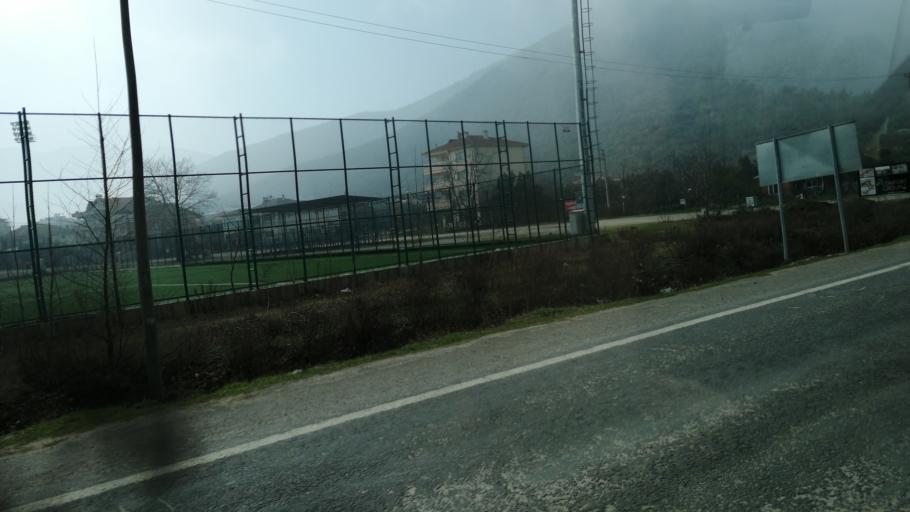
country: TR
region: Yalova
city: Cinarcik
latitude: 40.6354
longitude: 29.0793
